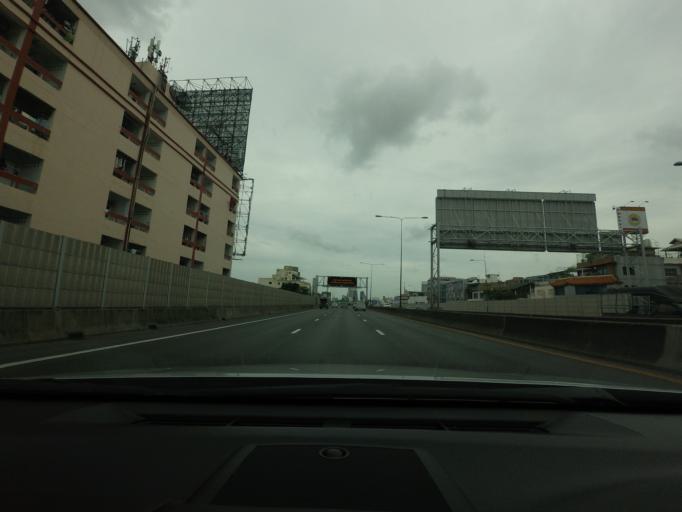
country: TH
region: Bangkok
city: Pathum Wan
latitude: 13.7444
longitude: 100.5205
